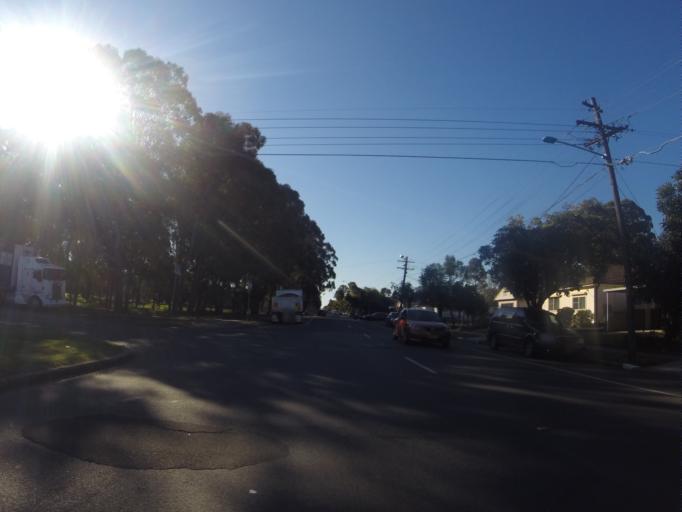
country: AU
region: New South Wales
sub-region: Bankstown
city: Regents Park
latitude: -33.8711
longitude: 151.0171
